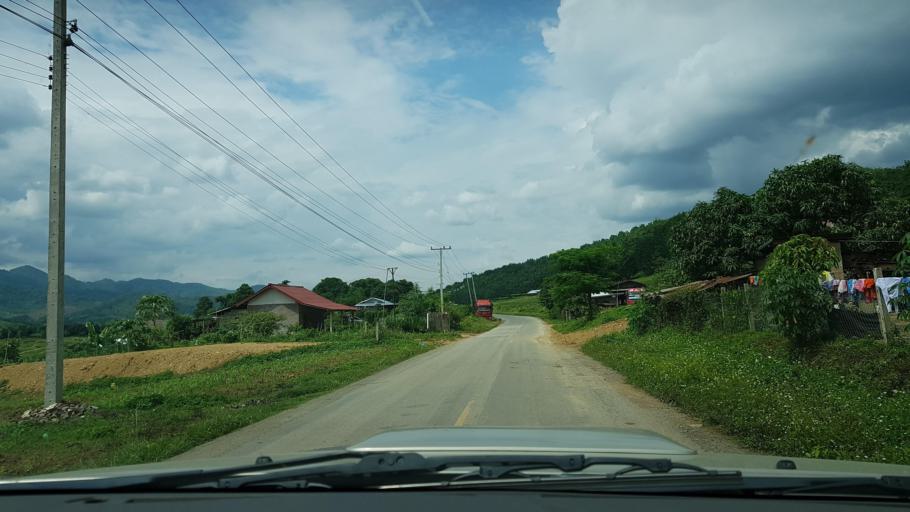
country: LA
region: Loungnamtha
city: Muang Nale
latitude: 20.2580
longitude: 101.5904
